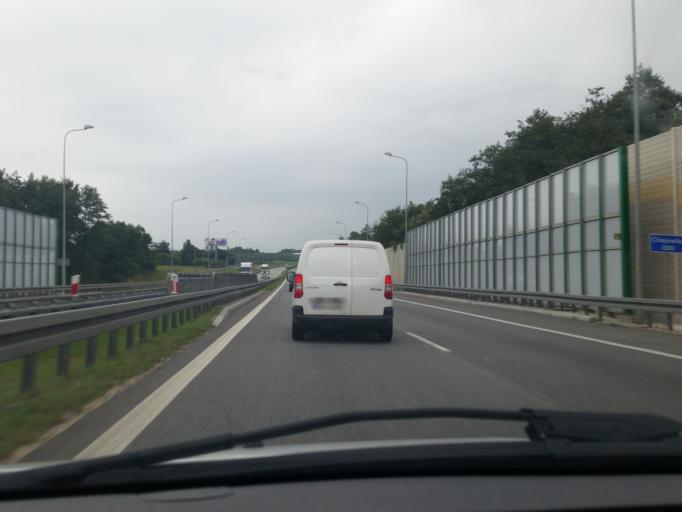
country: PL
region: Lodz Voivodeship
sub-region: Powiat skierniewicki
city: Kowiesy
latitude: 51.8889
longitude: 20.4186
